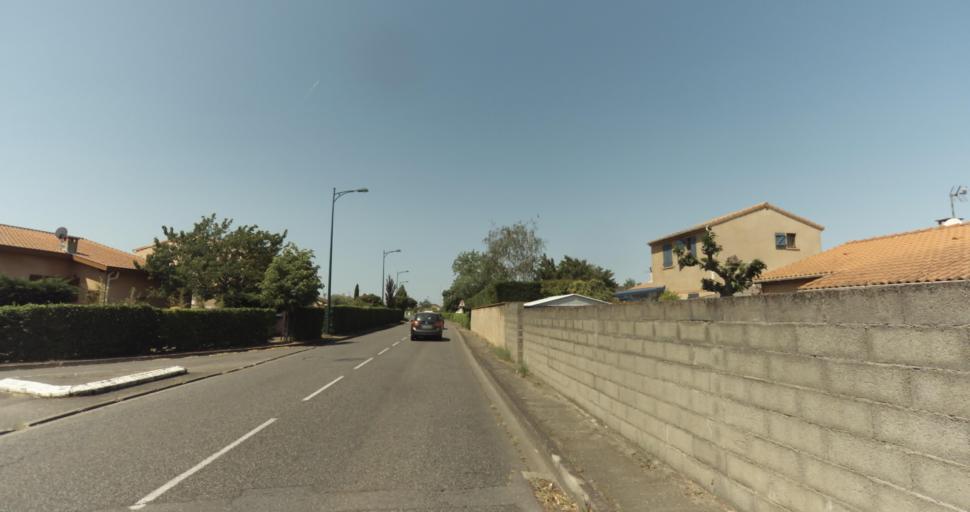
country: FR
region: Midi-Pyrenees
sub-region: Departement de la Haute-Garonne
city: Plaisance-du-Touch
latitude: 43.5614
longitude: 1.3078
